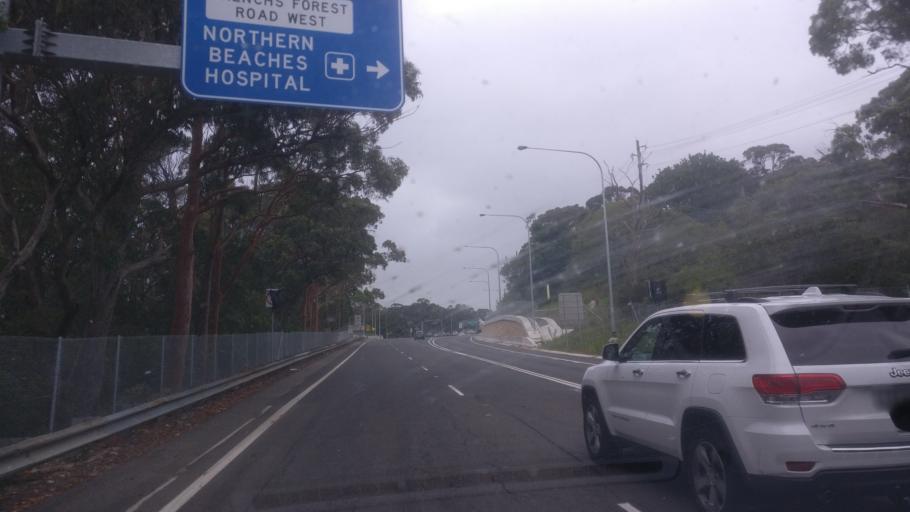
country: AU
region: New South Wales
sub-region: Warringah
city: Allambie Heights
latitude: -33.7474
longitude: 151.2345
